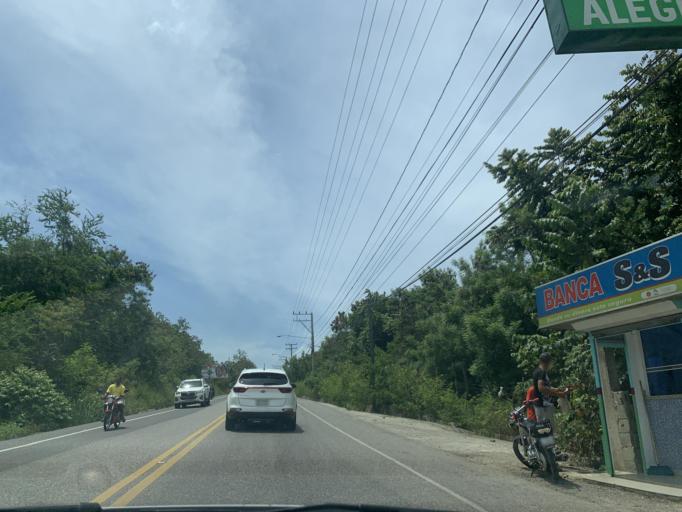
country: DO
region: Puerto Plata
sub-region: Puerto Plata
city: Puerto Plata
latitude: 19.7236
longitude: -70.6220
